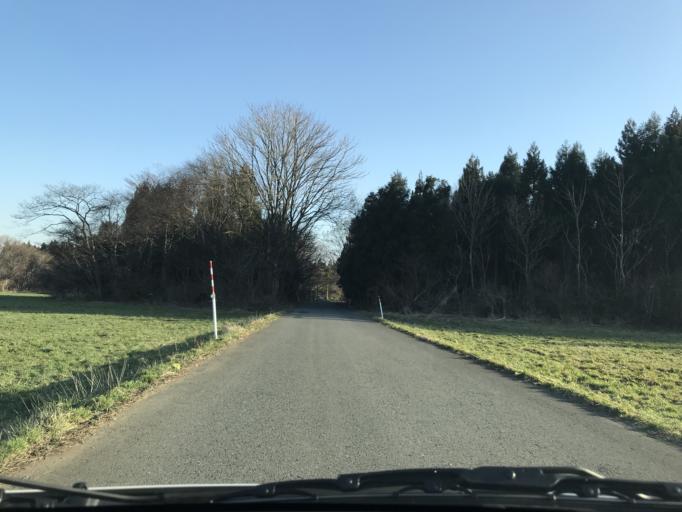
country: JP
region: Iwate
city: Kitakami
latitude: 39.2241
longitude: 141.0419
